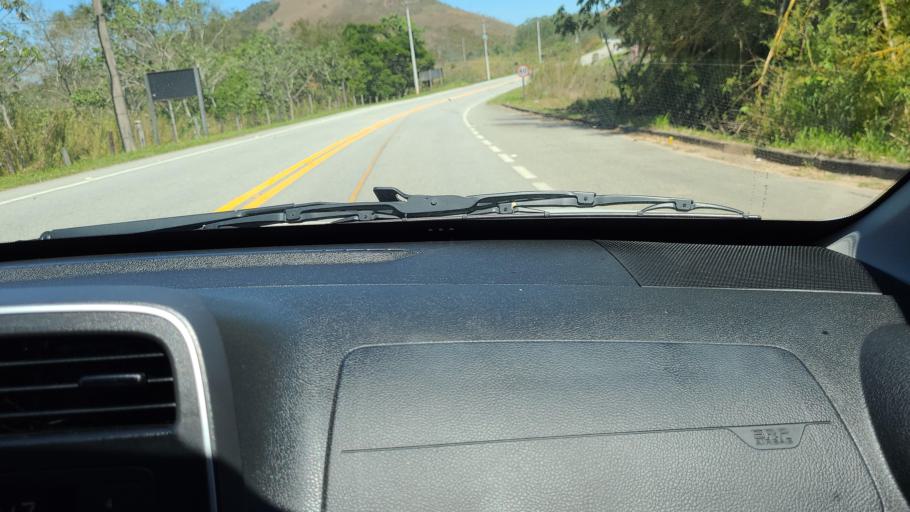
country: BR
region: Sao Paulo
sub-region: Tremembe
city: Tremembe
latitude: -22.8645
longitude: -45.5958
